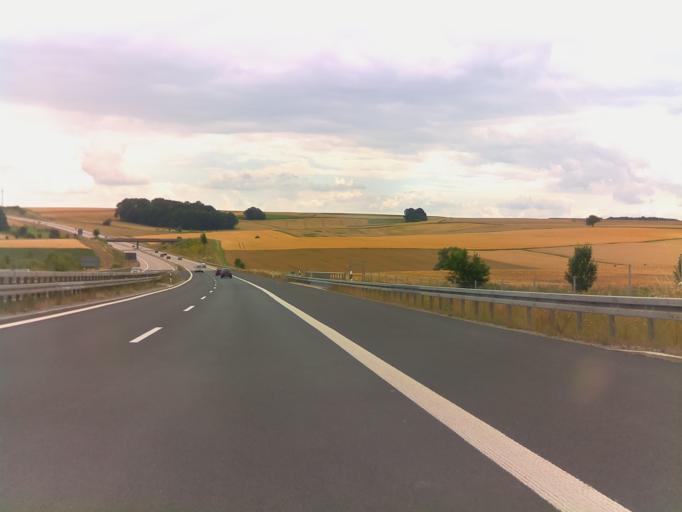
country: DE
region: Bavaria
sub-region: Regierungsbezirk Unterfranken
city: Oberstreu
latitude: 50.3900
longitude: 10.3137
